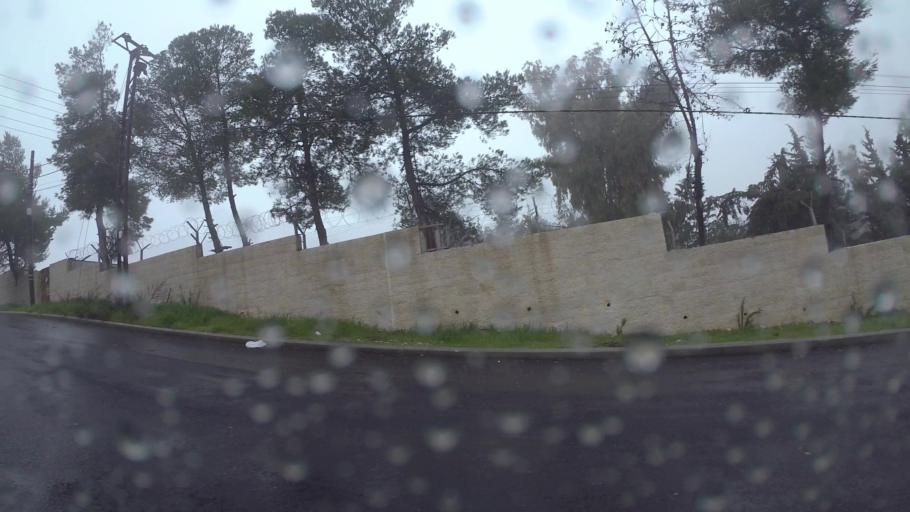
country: JO
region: Amman
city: Al Jubayhah
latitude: 32.0008
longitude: 35.8228
